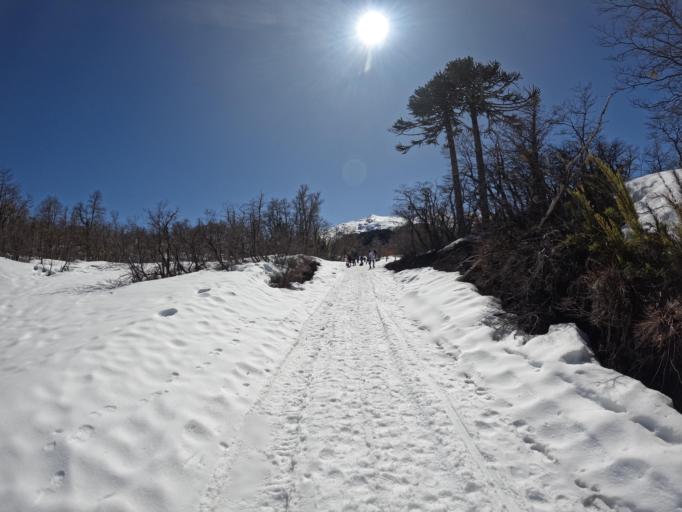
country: CL
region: Araucania
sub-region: Provincia de Cautin
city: Vilcun
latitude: -38.6588
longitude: -71.6187
